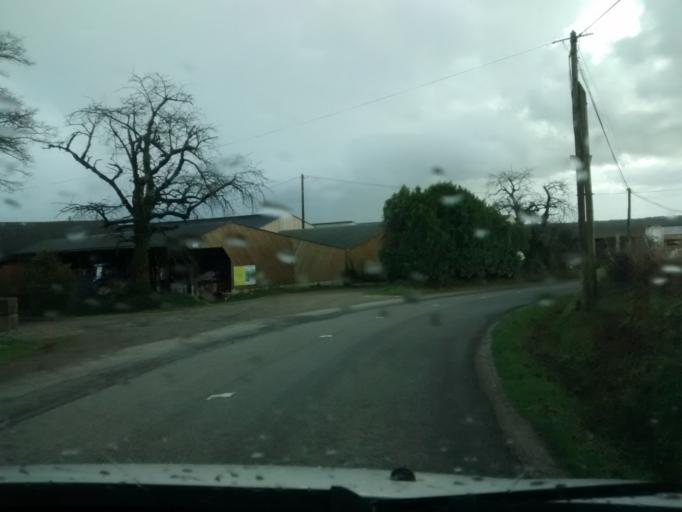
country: FR
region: Brittany
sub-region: Departement d'Ille-et-Vilaine
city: Liffre
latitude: 48.1869
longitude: -1.5042
